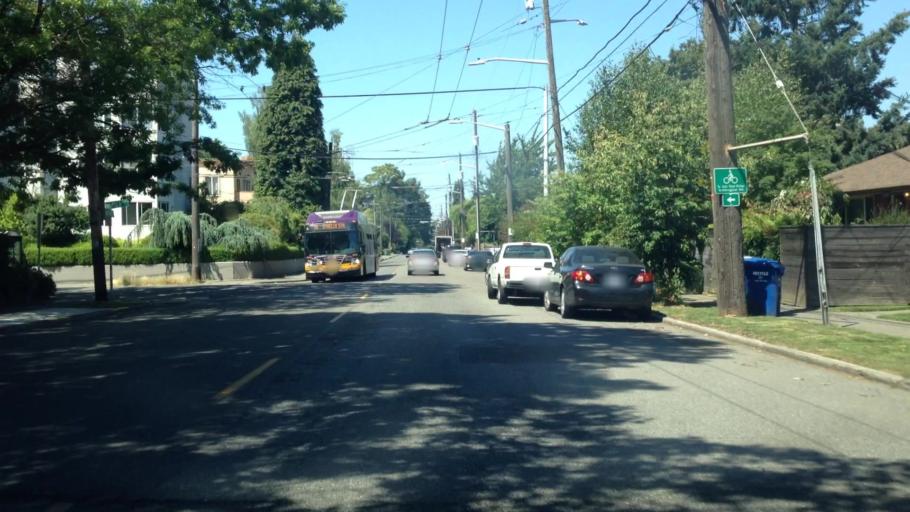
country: US
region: Washington
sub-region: King County
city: Seattle
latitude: 47.5881
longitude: -122.3149
